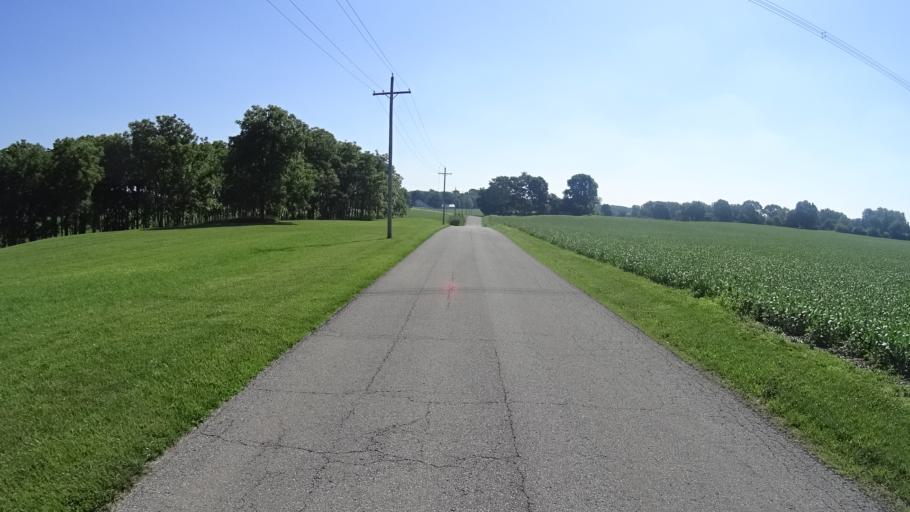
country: US
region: Indiana
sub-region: Madison County
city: Ingalls
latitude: 39.9645
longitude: -85.7949
